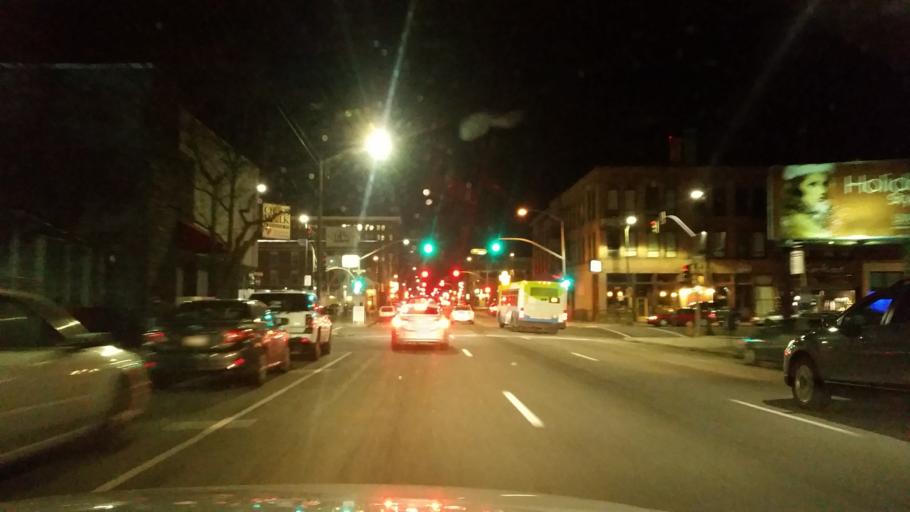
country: US
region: Washington
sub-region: Spokane County
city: Spokane
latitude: 47.6545
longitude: -117.4204
